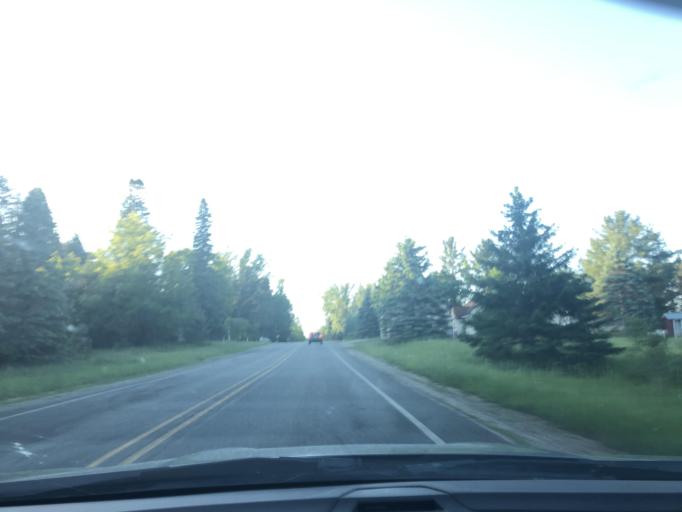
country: US
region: Michigan
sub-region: Missaukee County
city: Lake City
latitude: 44.4488
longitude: -85.0748
